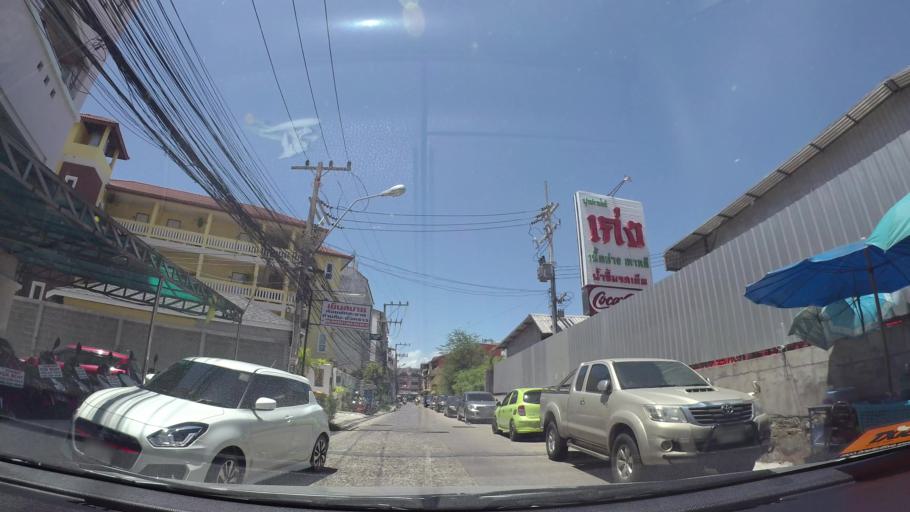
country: TH
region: Chon Buri
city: Phatthaya
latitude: 12.9214
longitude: 100.8771
